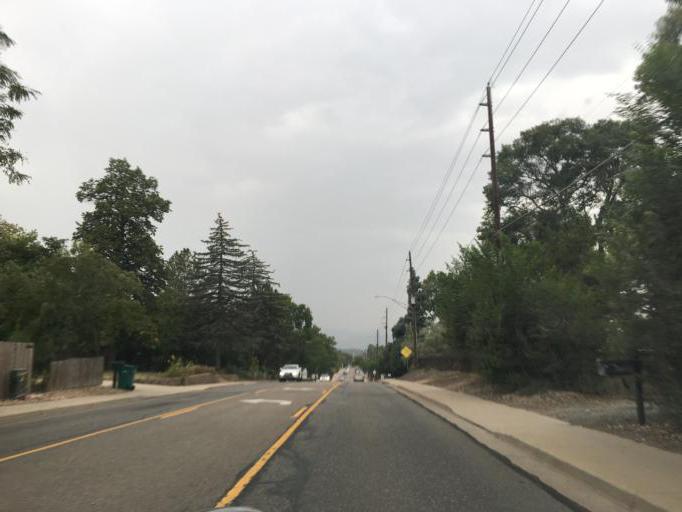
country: US
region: Colorado
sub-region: Jefferson County
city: Wheat Ridge
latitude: 39.7694
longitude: -105.0938
